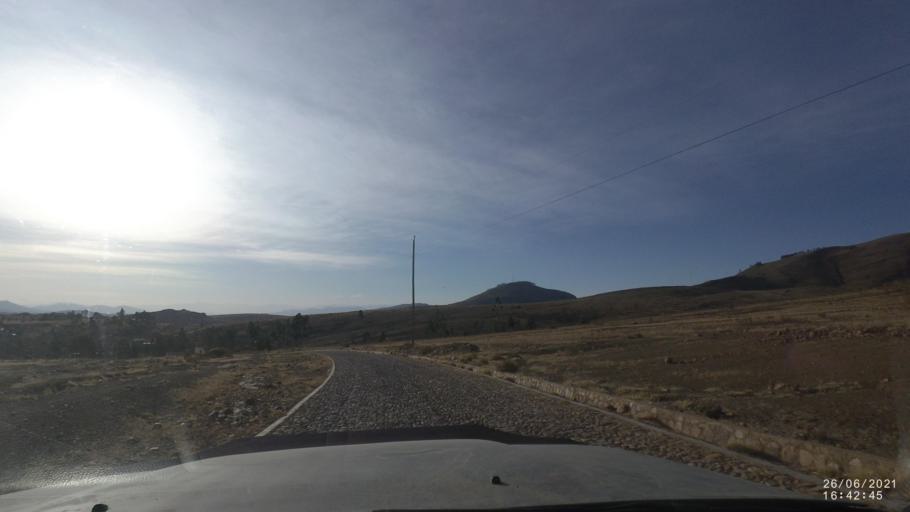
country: BO
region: Cochabamba
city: Arani
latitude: -17.7624
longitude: -65.8280
